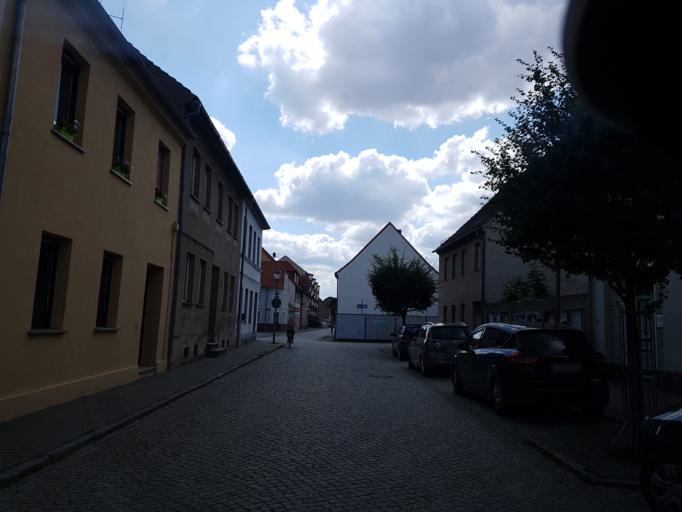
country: DE
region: Brandenburg
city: Drebkau
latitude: 51.6575
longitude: 14.2201
